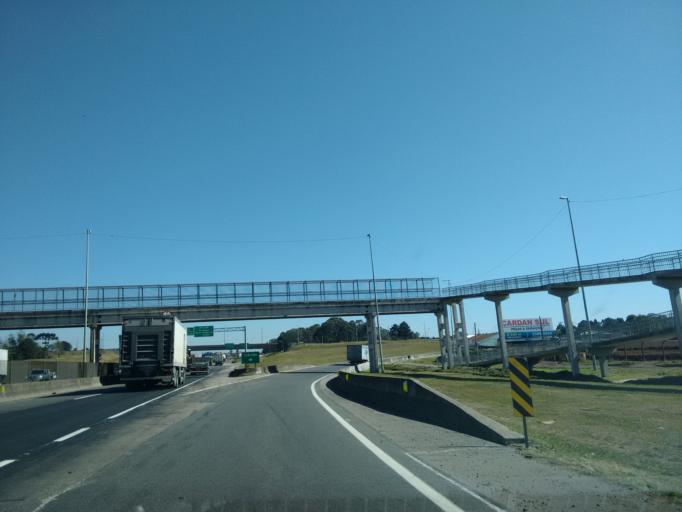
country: BR
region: Parana
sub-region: Sao Jose Dos Pinhais
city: Sao Jose dos Pinhais
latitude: -25.5450
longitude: -49.2993
